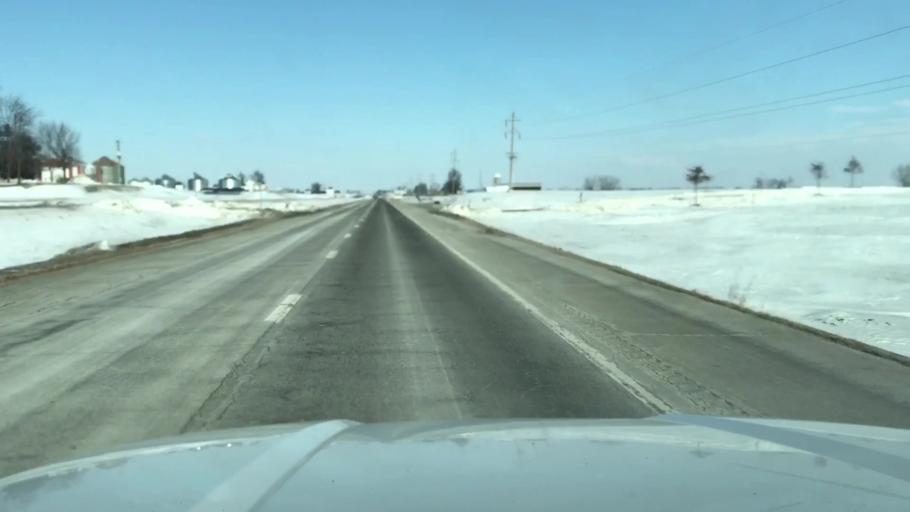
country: US
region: Missouri
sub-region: Nodaway County
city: Maryville
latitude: 40.2383
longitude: -94.8674
